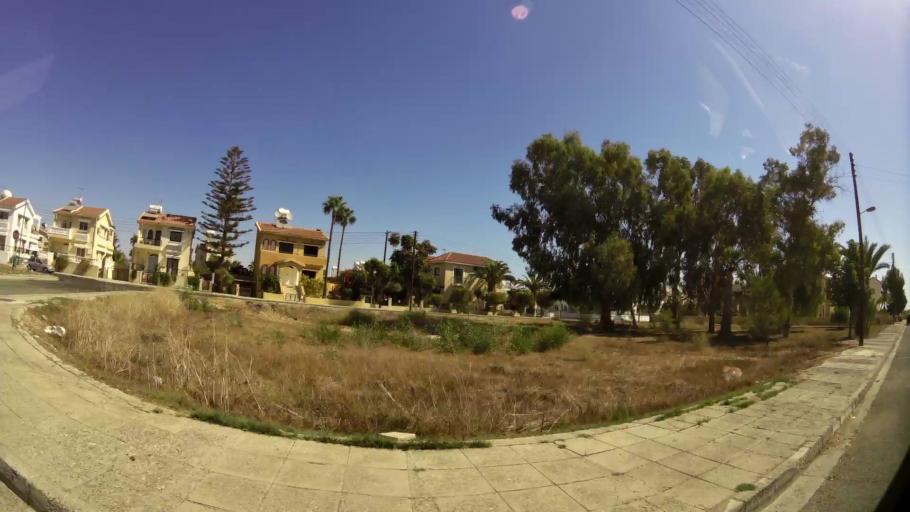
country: CY
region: Larnaka
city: Voroklini
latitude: 34.9594
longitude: 33.6528
